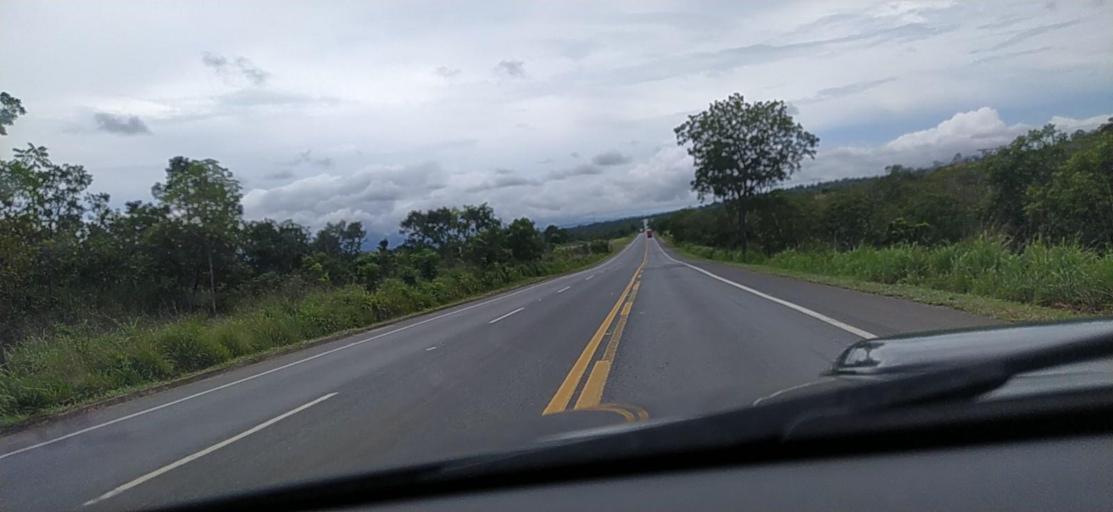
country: BR
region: Minas Gerais
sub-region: Corinto
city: Corinto
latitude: -18.3187
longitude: -44.4243
